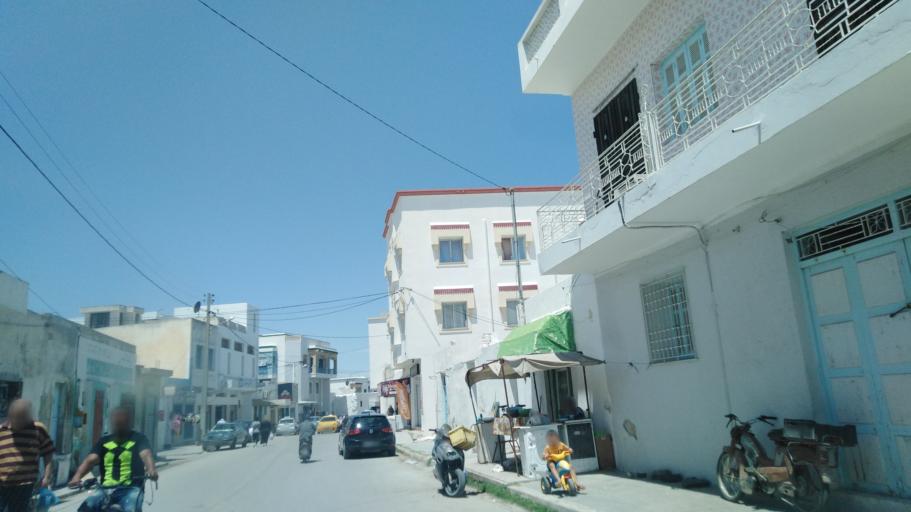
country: TN
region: Al Mahdiyah
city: Ksour Essaf
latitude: 35.4169
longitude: 10.9938
